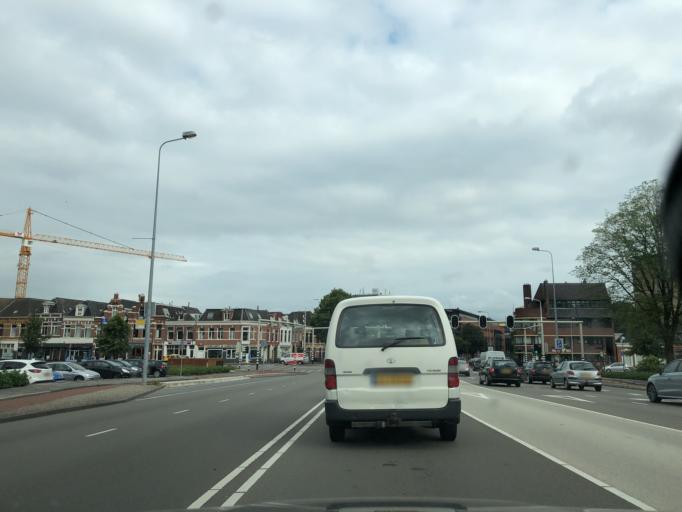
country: NL
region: Groningen
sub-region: Gemeente Groningen
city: Oosterpark
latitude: 53.2179
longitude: 6.5792
